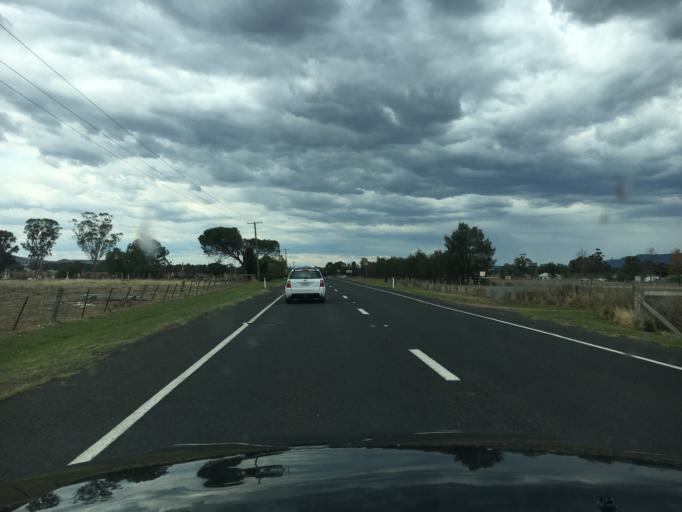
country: AU
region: New South Wales
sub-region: Muswellbrook
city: Muswellbrook
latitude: -32.0262
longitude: 150.8634
